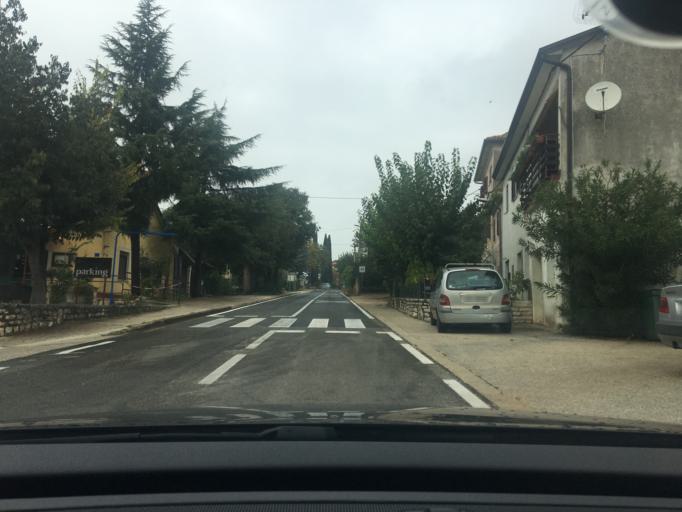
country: HR
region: Istarska
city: Buje
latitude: 45.4424
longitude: 13.6565
